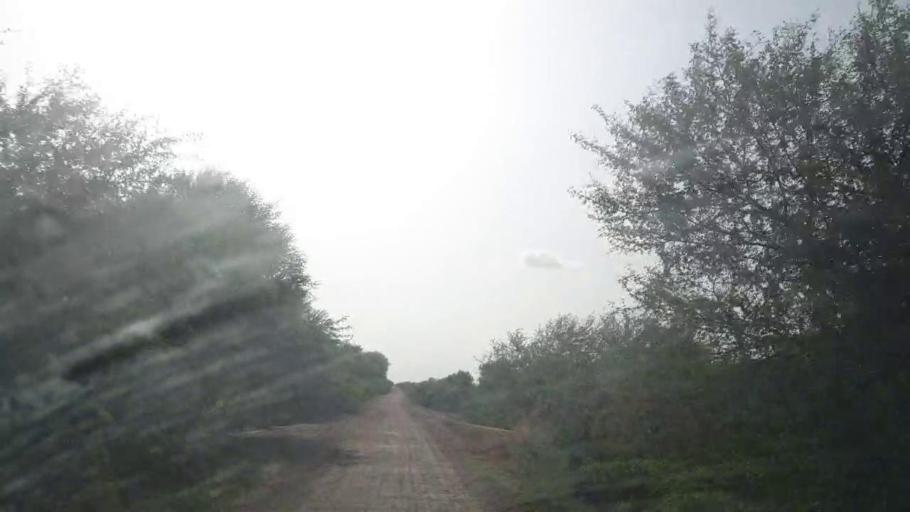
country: PK
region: Sindh
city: Tando Bago
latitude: 24.8241
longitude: 69.1261
